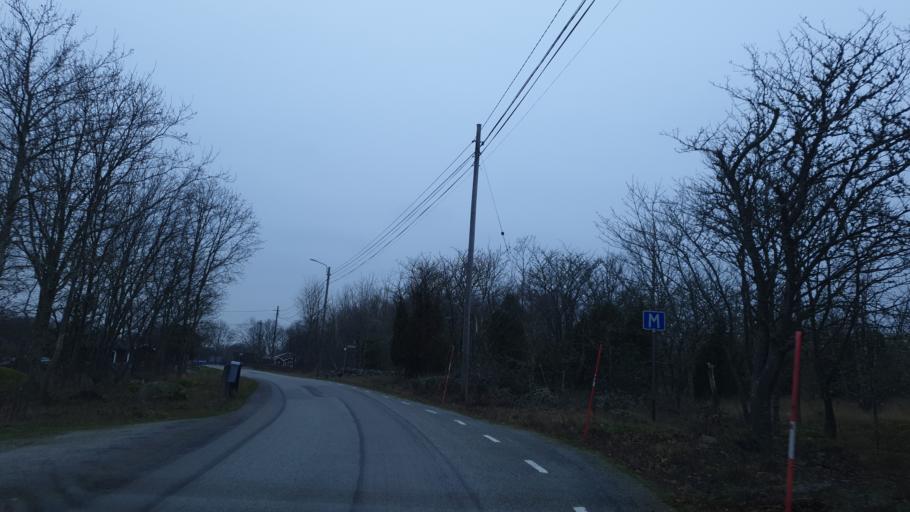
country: SE
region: Blekinge
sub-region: Karlskrona Kommun
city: Karlskrona
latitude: 56.1091
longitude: 15.6087
